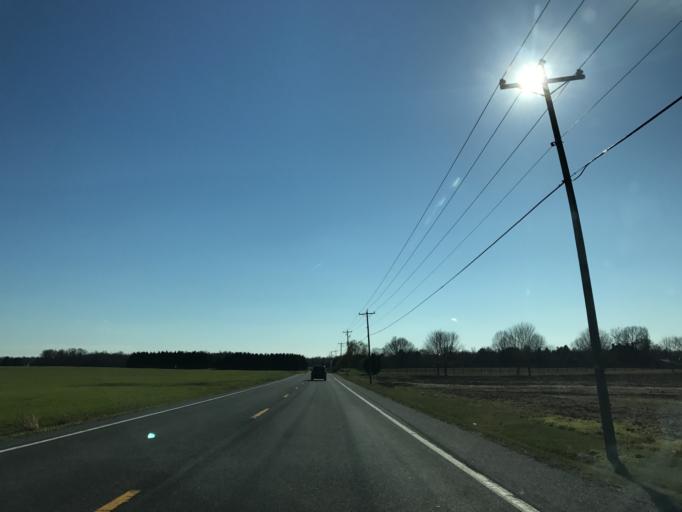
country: US
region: Maryland
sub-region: Caroline County
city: Ridgely
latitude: 39.0159
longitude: -75.9279
